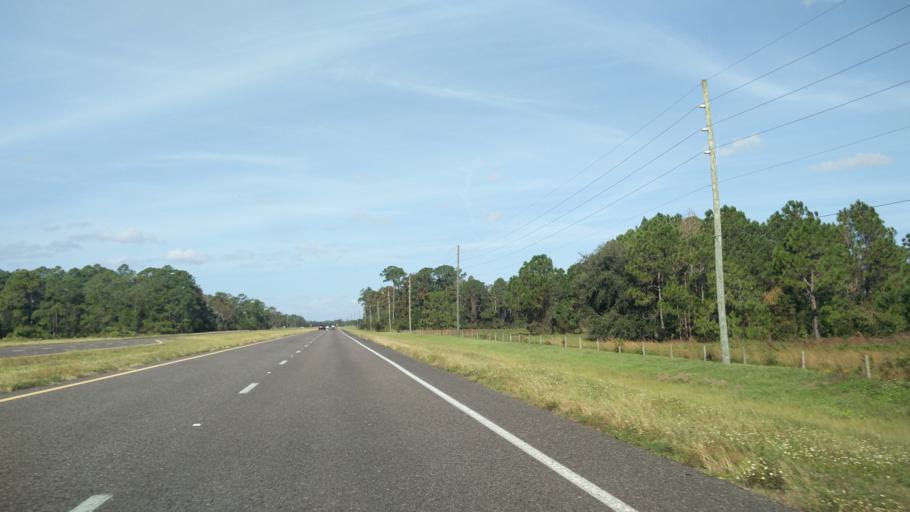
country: US
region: Florida
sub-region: Brevard County
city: June Park
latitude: 28.1089
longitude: -80.9131
